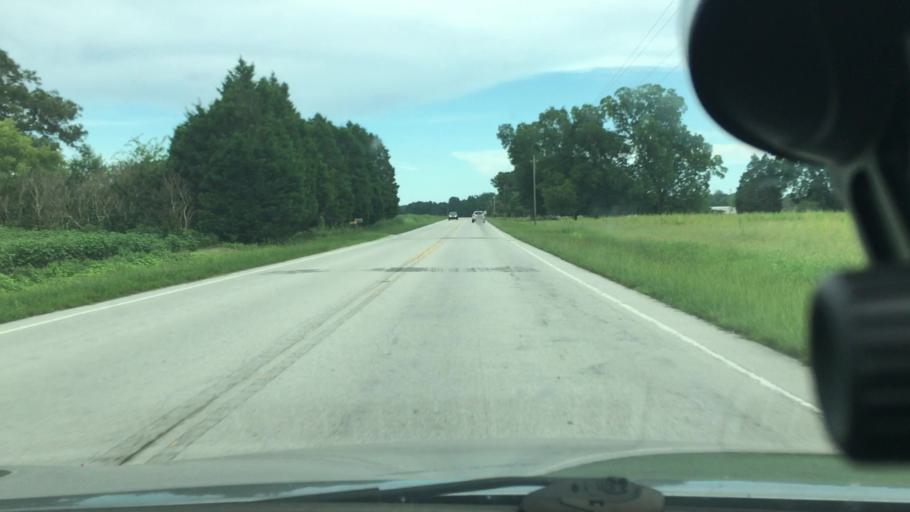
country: US
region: North Carolina
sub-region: Craven County
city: Vanceboro
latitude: 35.3763
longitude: -77.2145
